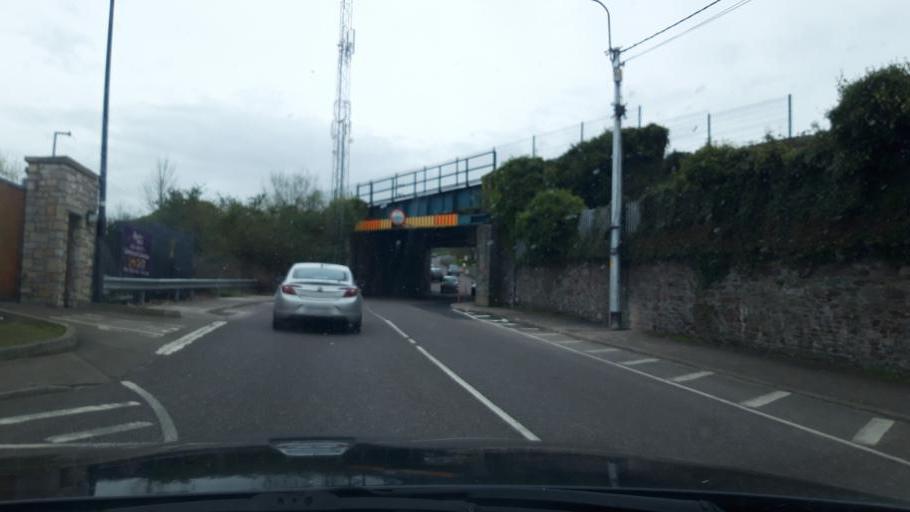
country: IE
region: Munster
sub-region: County Cork
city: Cork
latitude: 51.9158
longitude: -8.4697
